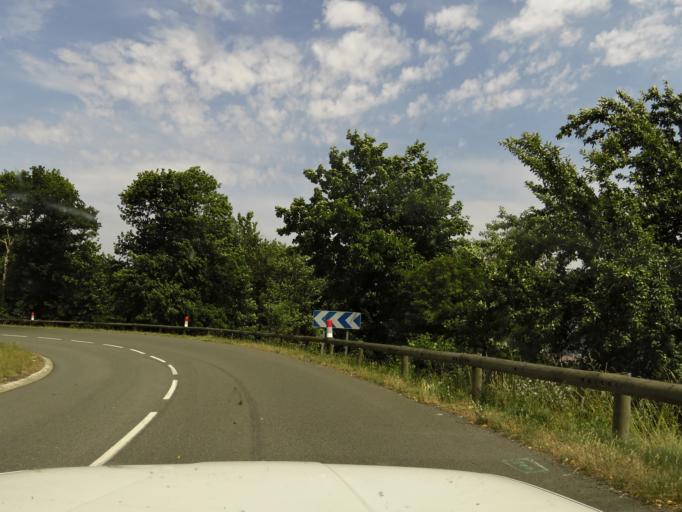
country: FR
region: Auvergne
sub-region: Departement du Puy-de-Dome
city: Orcines
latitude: 45.7674
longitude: 3.0212
